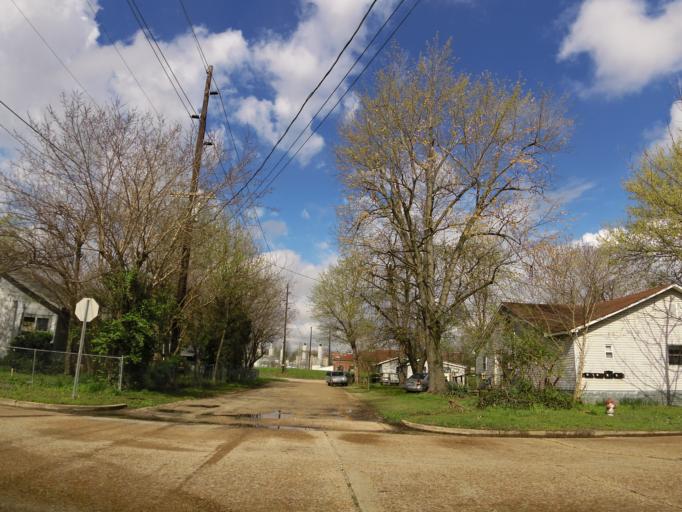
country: US
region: Missouri
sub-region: Butler County
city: Poplar Bluff
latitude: 36.7592
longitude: -90.3865
